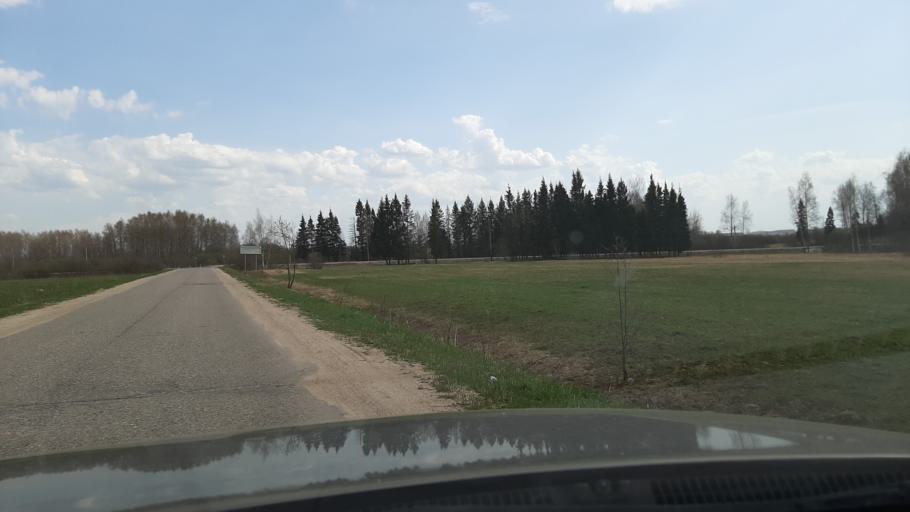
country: RU
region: Ivanovo
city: Furmanov
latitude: 57.2948
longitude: 41.1763
